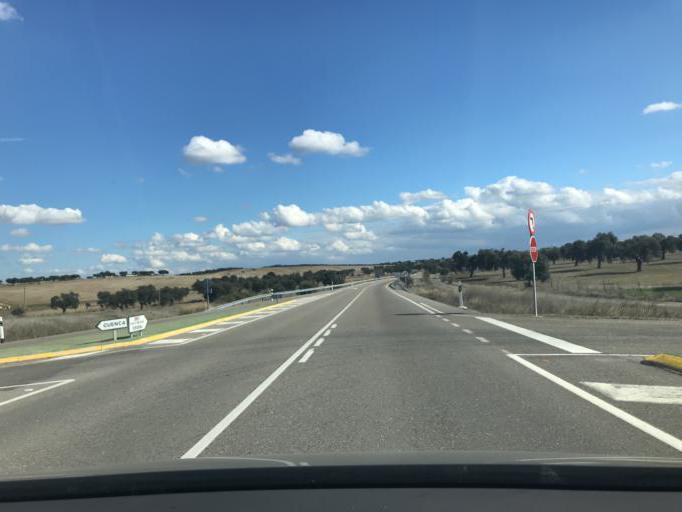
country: ES
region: Extremadura
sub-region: Provincia de Badajoz
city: Granja de Torrehermosa
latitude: 38.2884
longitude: -5.5266
